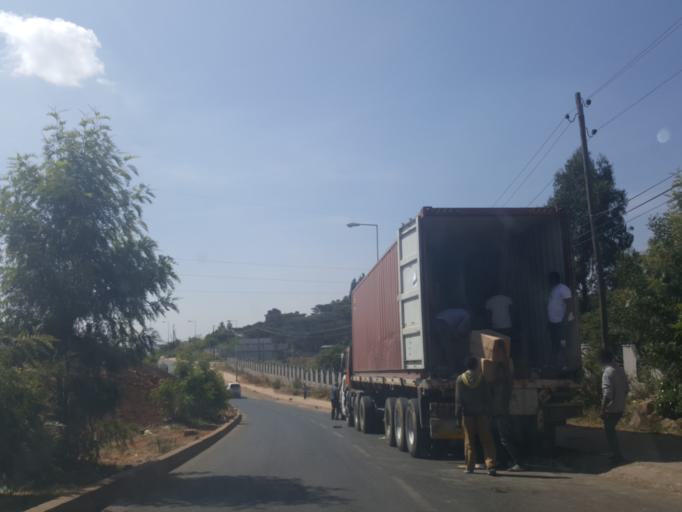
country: ET
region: Adis Abeba
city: Addis Ababa
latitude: 9.0670
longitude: 38.7150
